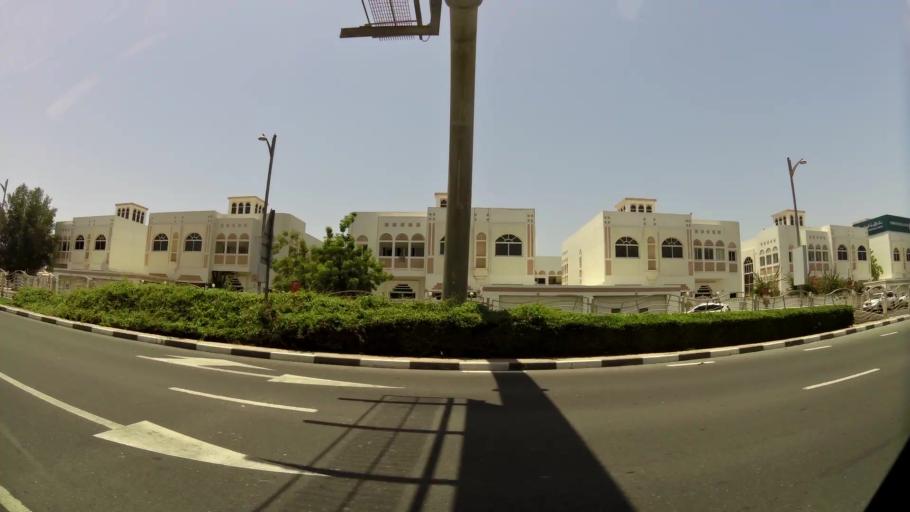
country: AE
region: Dubai
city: Dubai
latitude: 25.2223
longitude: 55.2564
